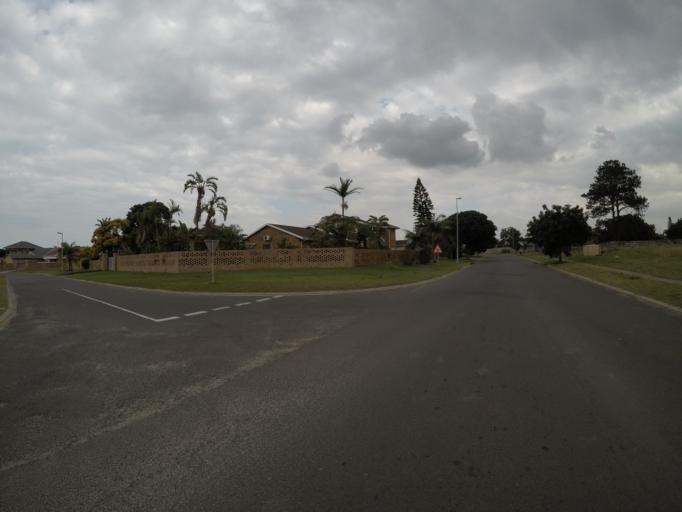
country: ZA
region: KwaZulu-Natal
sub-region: uThungulu District Municipality
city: Richards Bay
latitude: -28.7360
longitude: 32.0492
